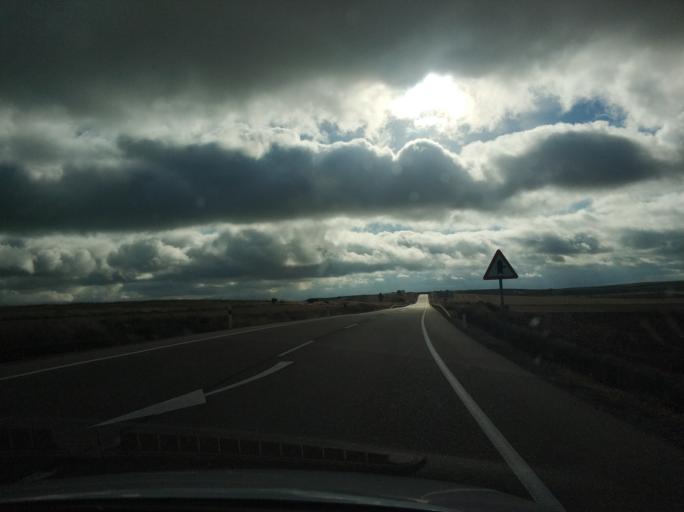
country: ES
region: Castille and Leon
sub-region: Provincia de Soria
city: Fuentecambron
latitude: 41.4714
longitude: -3.3243
